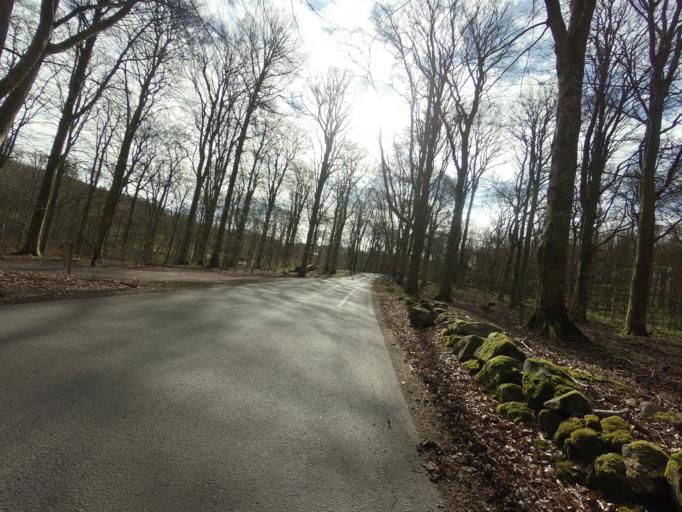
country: SE
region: Skane
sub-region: Hoganas Kommun
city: Hoganas
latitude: 56.2959
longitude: 12.4812
